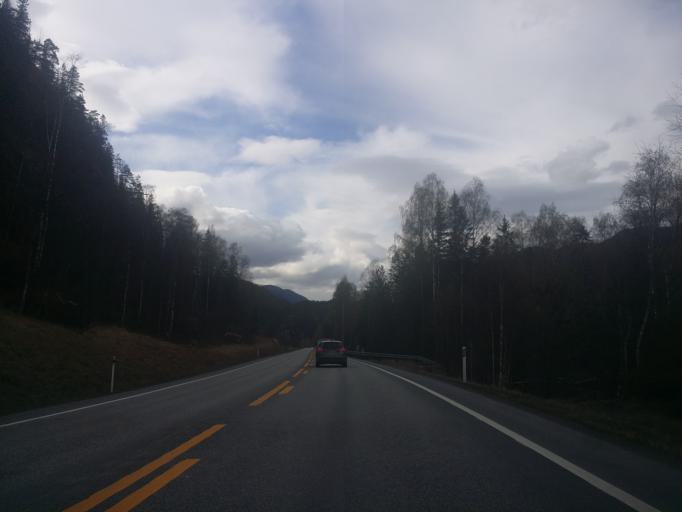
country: NO
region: Buskerud
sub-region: Nes
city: Nesbyen
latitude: 60.4642
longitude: 9.2517
